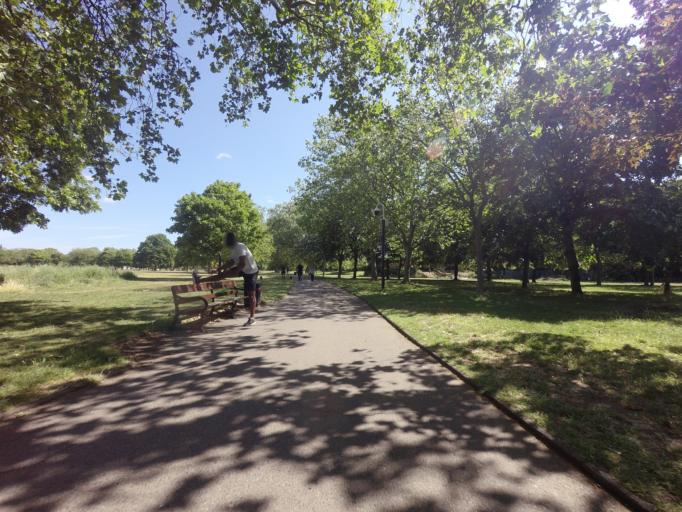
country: GB
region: England
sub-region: Greater London
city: East Ham
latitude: 51.5374
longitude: 0.0150
